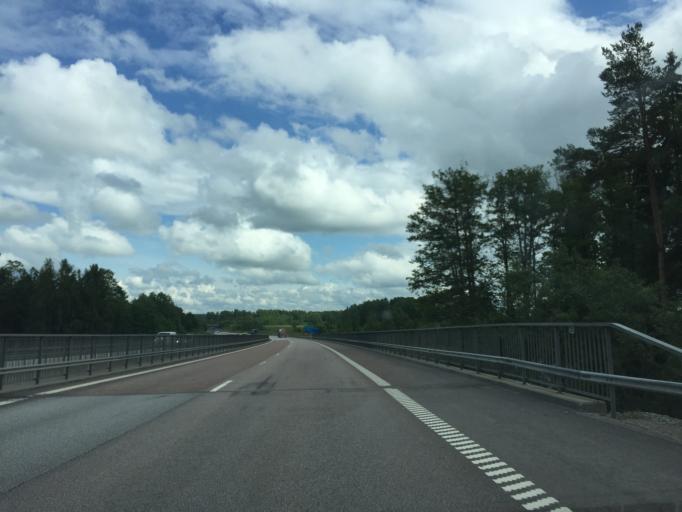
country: SE
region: Vaestmanland
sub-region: Arboga Kommun
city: Arboga
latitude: 59.4059
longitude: 15.7578
